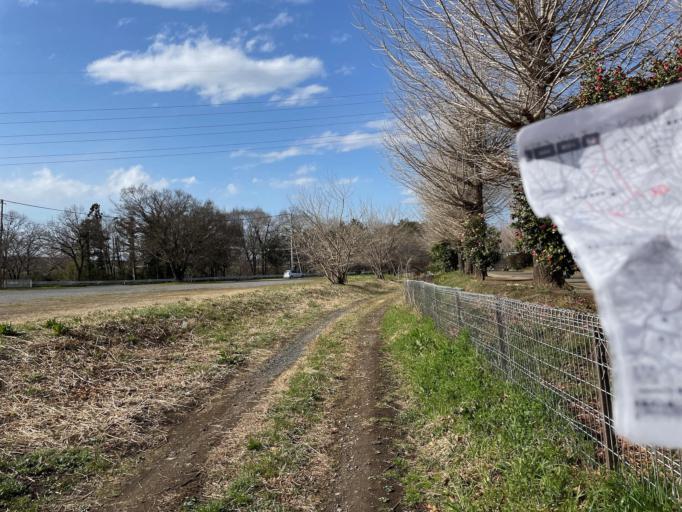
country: JP
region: Saitama
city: Sakado
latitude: 35.9585
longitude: 139.3438
